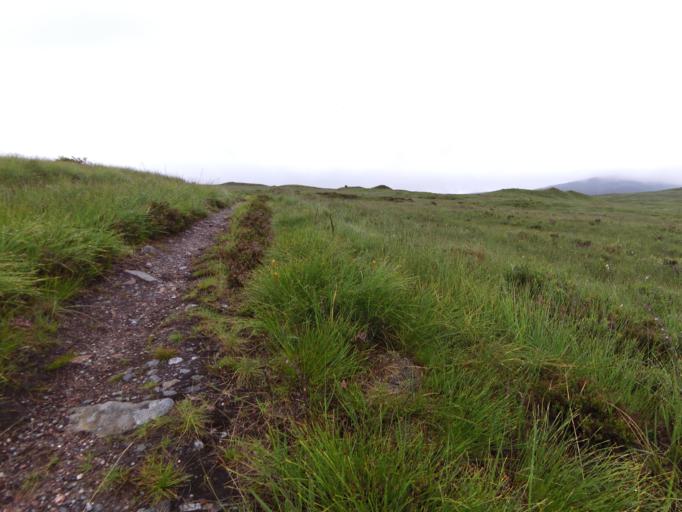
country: GB
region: Scotland
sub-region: Highland
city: Spean Bridge
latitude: 56.7690
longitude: -4.7052
